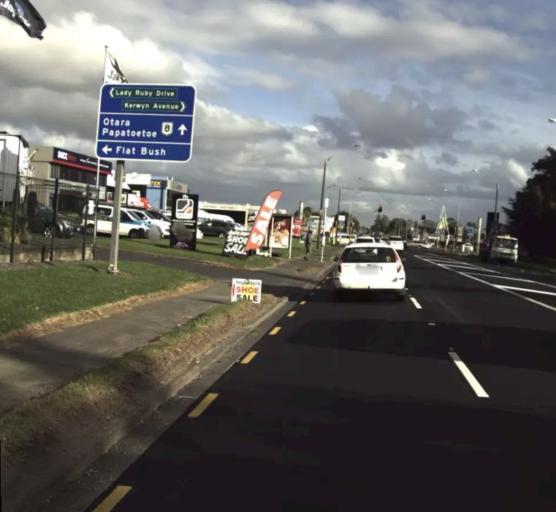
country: NZ
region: Auckland
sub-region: Auckland
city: Manukau City
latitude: -36.9474
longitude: 174.8927
